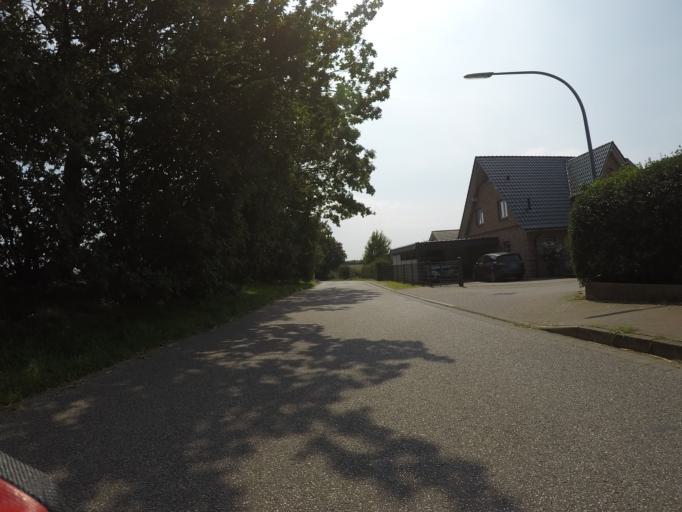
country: DE
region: Schleswig-Holstein
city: Kisdorf
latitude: 53.8051
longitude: 10.0129
